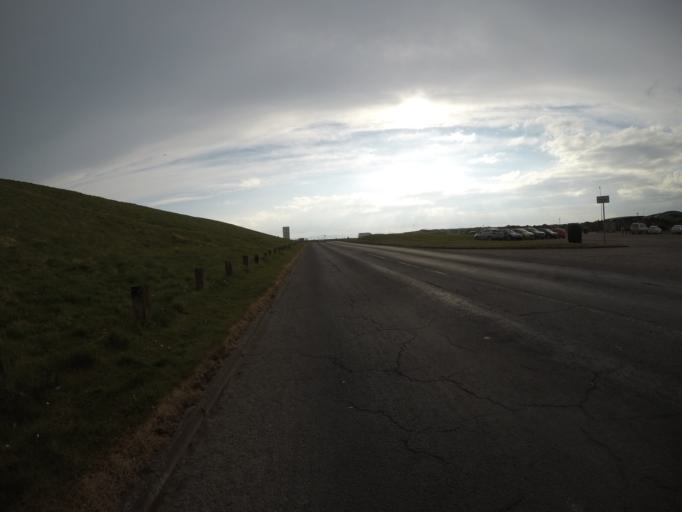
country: GB
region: Scotland
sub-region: North Ayrshire
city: Irvine
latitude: 55.6068
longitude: -4.6902
